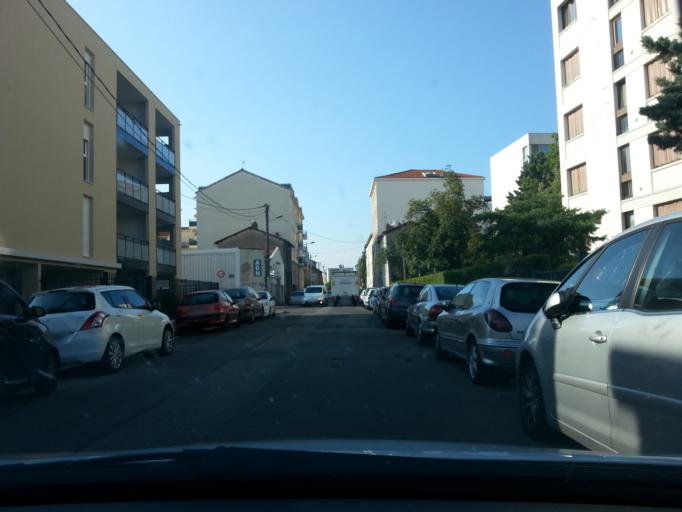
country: FR
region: Rhone-Alpes
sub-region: Departement du Rhone
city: Saint-Fons
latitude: 45.7284
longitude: 4.8574
